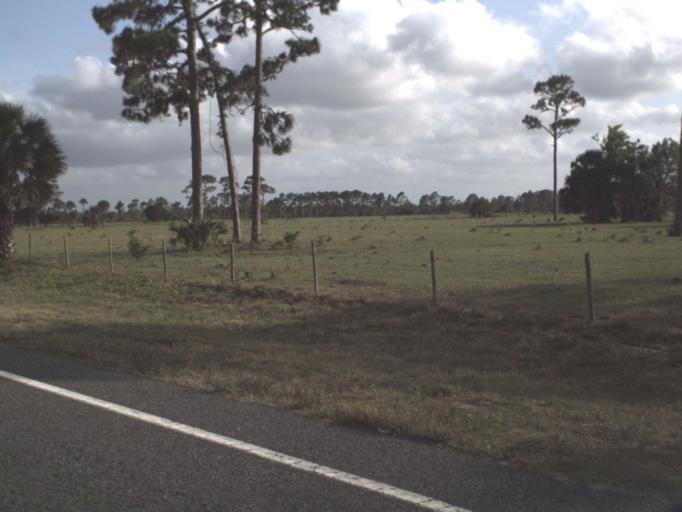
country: US
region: Florida
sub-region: Volusia County
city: Oak Hill
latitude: 28.7781
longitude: -80.8813
